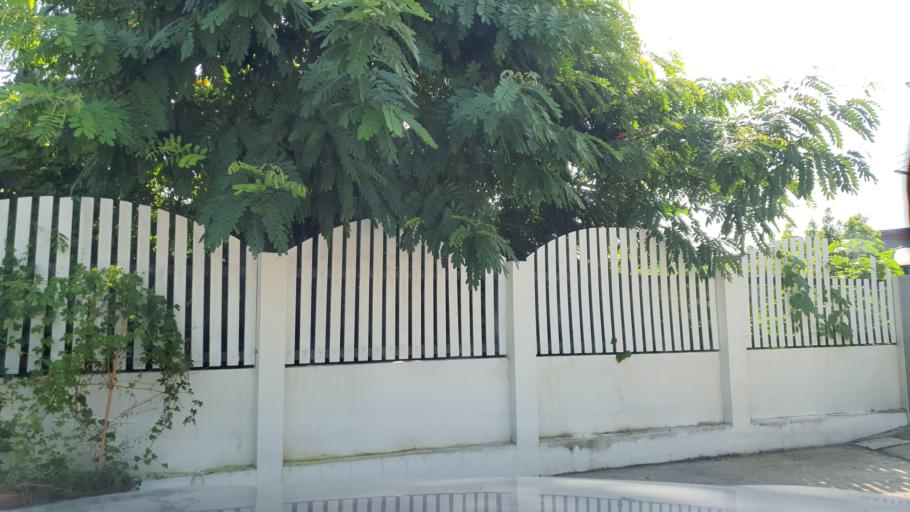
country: TH
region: Chiang Mai
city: Hang Dong
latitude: 18.7126
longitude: 98.9300
